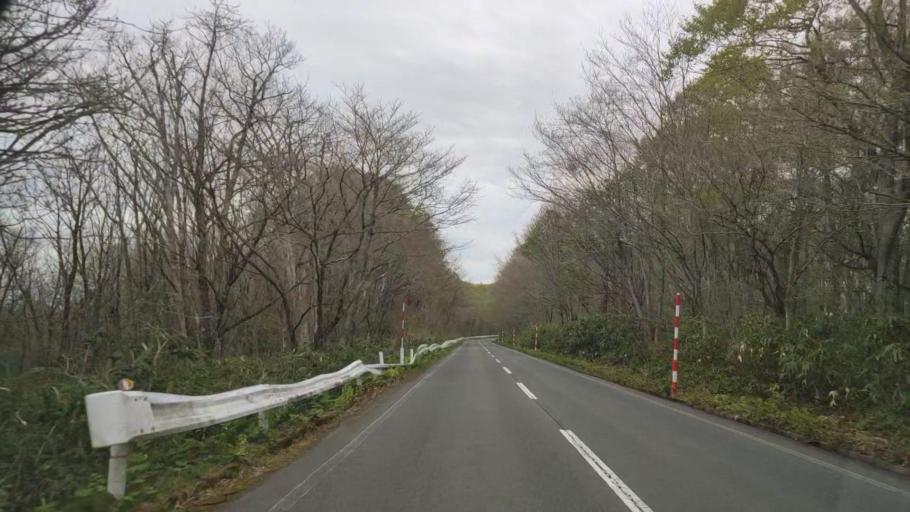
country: JP
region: Akita
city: Hanawa
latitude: 40.4036
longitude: 140.8076
